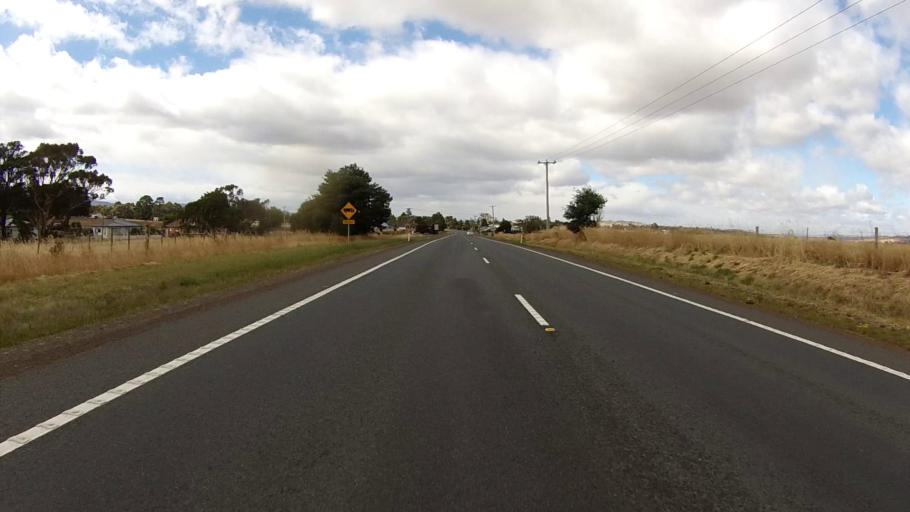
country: AU
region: Tasmania
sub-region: Northern Midlands
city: Evandale
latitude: -41.9132
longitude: 147.4829
